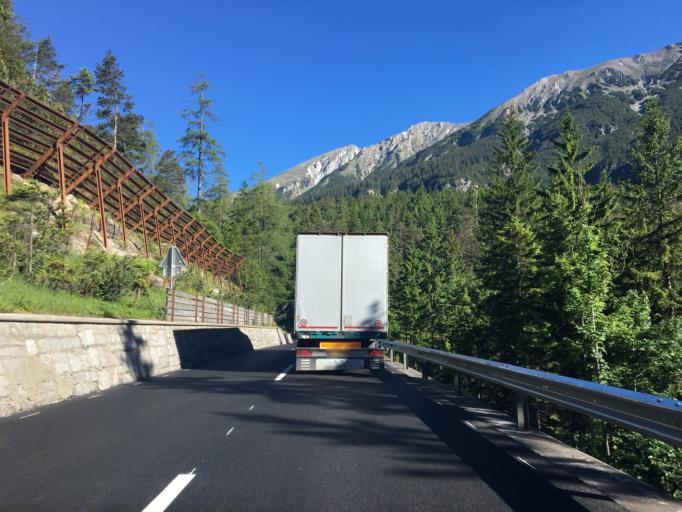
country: AT
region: Tyrol
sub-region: Politischer Bezirk Imst
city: Nassereith
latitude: 47.3635
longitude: 10.8400
